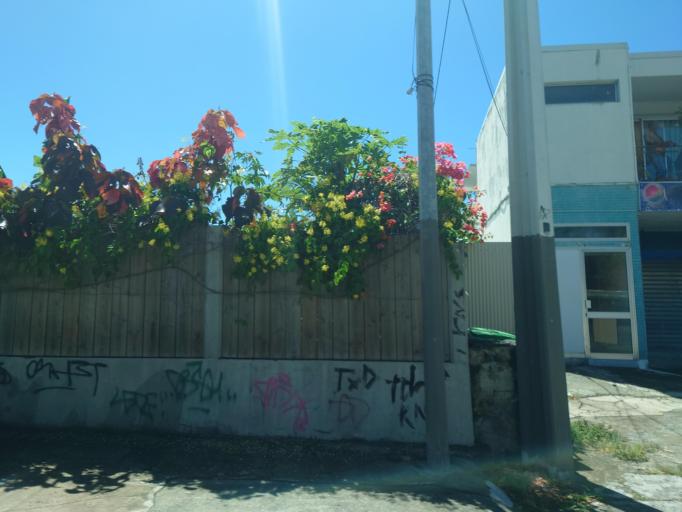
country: NC
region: South Province
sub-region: Noumea
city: Noumea
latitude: -22.2685
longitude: 166.4556
